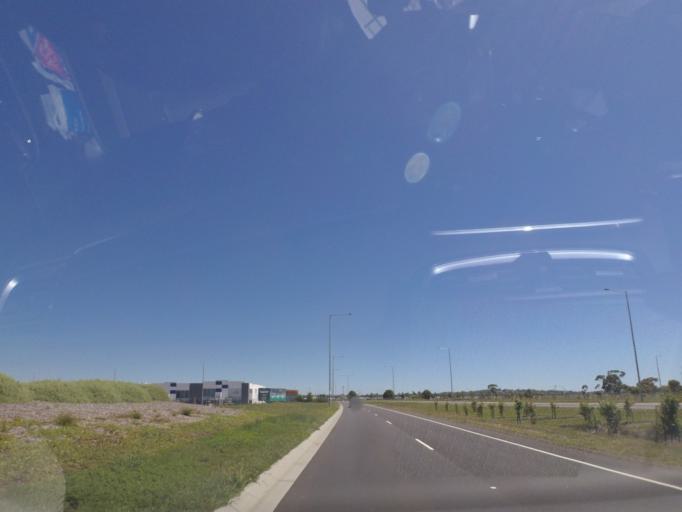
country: AU
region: Victoria
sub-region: Hume
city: Gladstone Park
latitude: -37.6860
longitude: 144.8650
